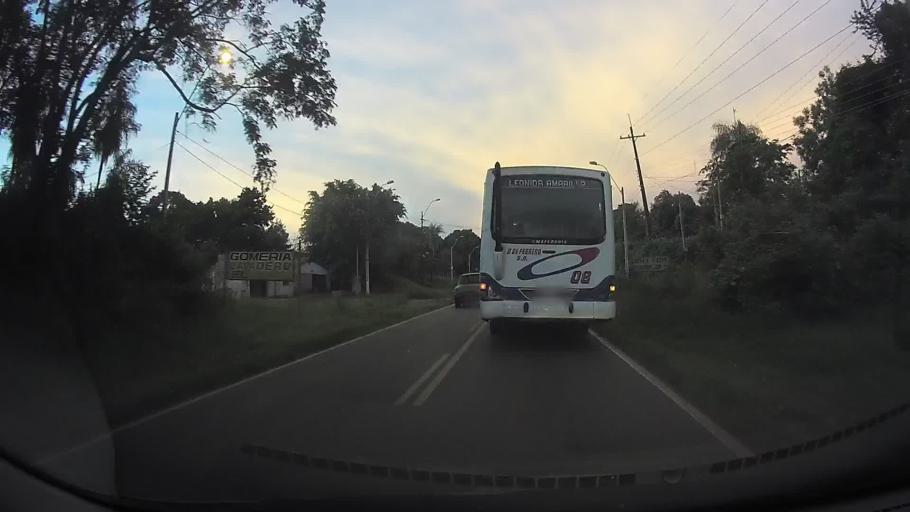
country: PY
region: Central
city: Ita
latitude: -25.4767
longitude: -57.3628
